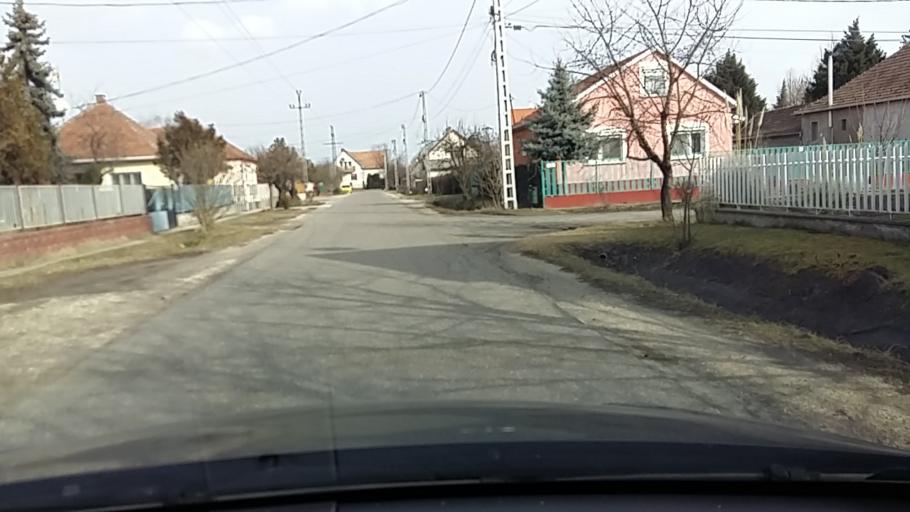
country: HU
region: Pest
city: Szigetszentmiklos
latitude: 47.3508
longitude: 19.0250
